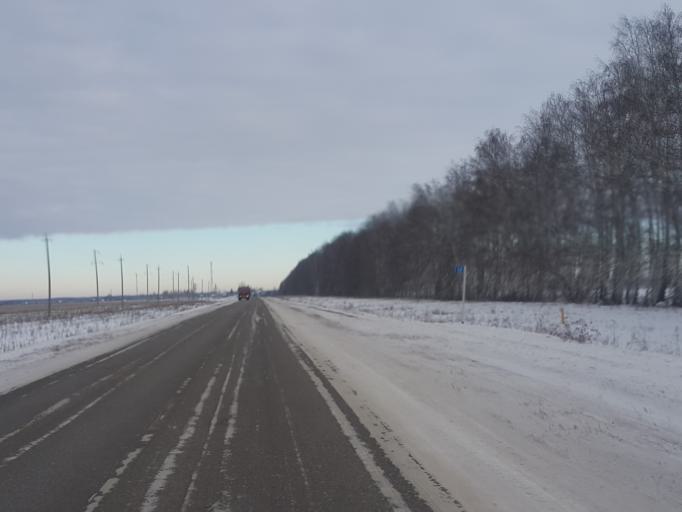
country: RU
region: Tambov
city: Rasskazovo
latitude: 52.8148
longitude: 41.7940
